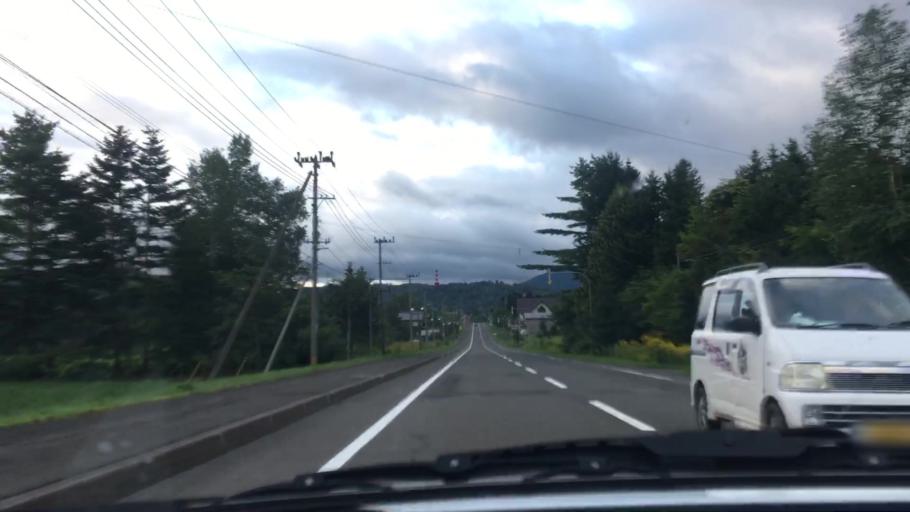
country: JP
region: Hokkaido
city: Shimo-furano
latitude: 42.9965
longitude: 142.4035
